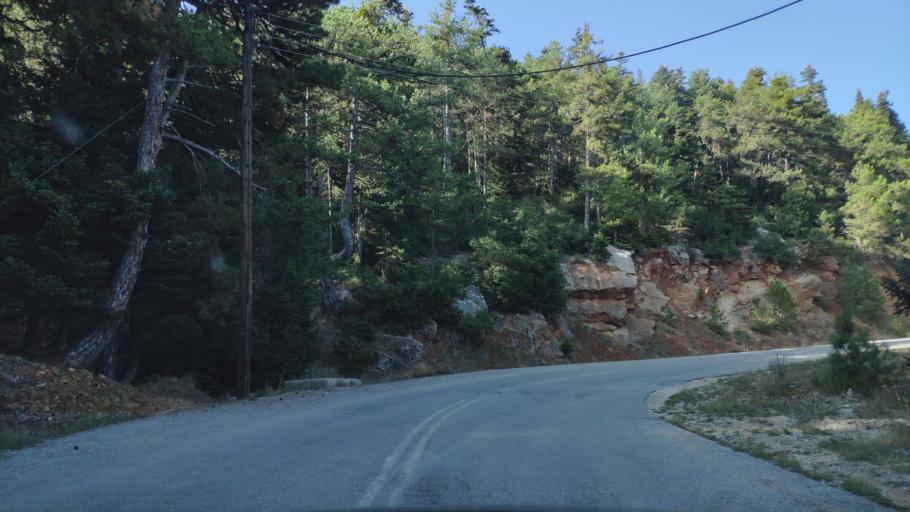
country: GR
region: West Greece
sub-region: Nomos Achaias
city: Aiyira
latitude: 38.0196
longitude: 22.4034
